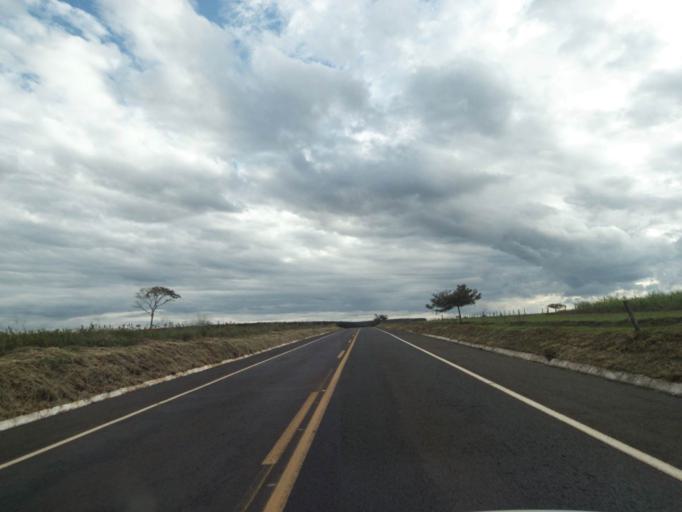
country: PY
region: Canindeyu
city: Salto del Guaira
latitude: -24.0837
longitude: -54.0720
